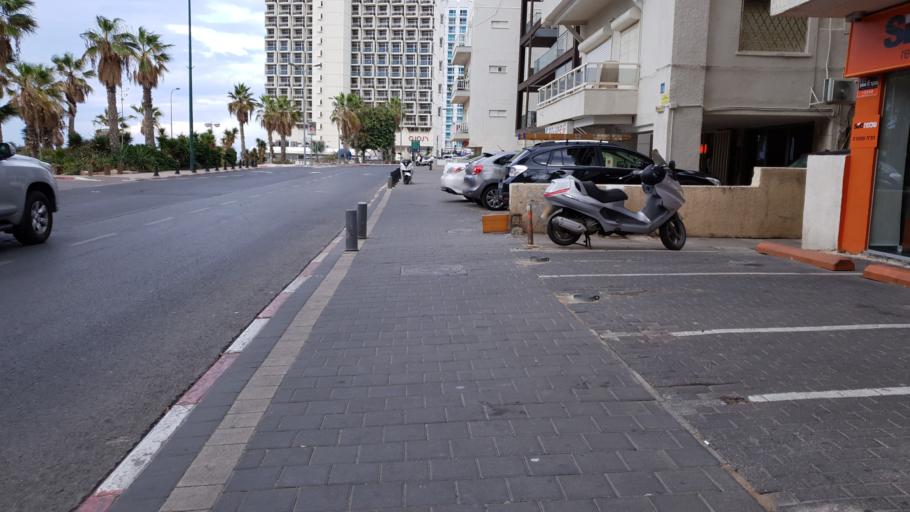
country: IL
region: Tel Aviv
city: Tel Aviv
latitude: 32.0815
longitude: 34.7684
